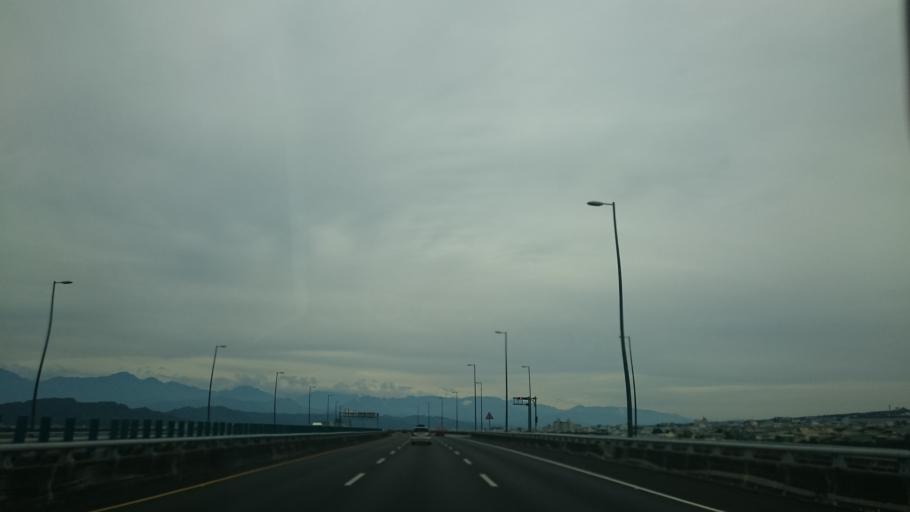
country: TW
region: Taiwan
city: Zhongxing New Village
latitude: 23.9455
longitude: 120.6707
